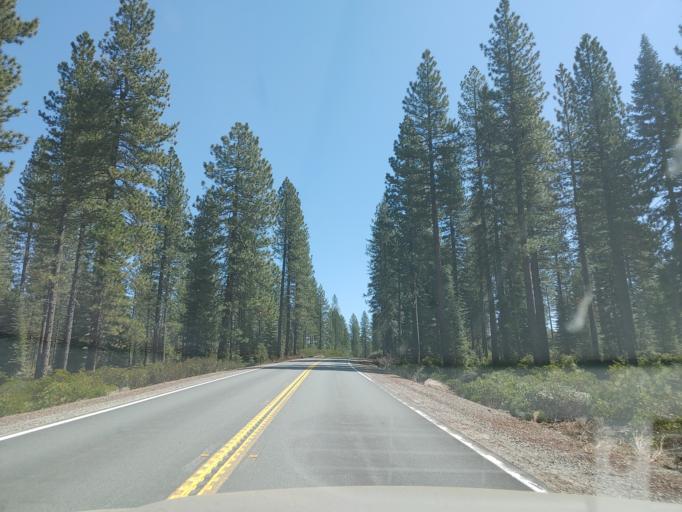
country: US
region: California
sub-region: Siskiyou County
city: McCloud
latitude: 41.2664
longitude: -121.8596
